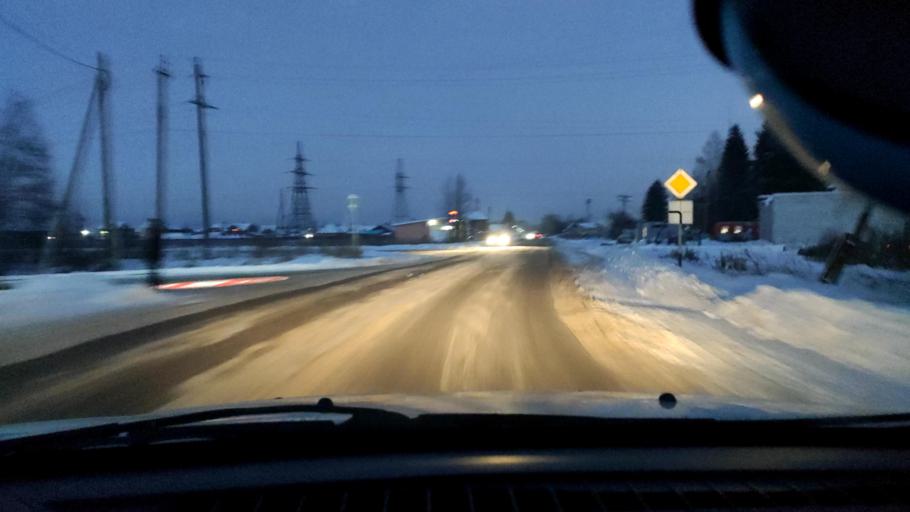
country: RU
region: Perm
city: Kultayevo
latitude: 57.8875
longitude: 55.9236
